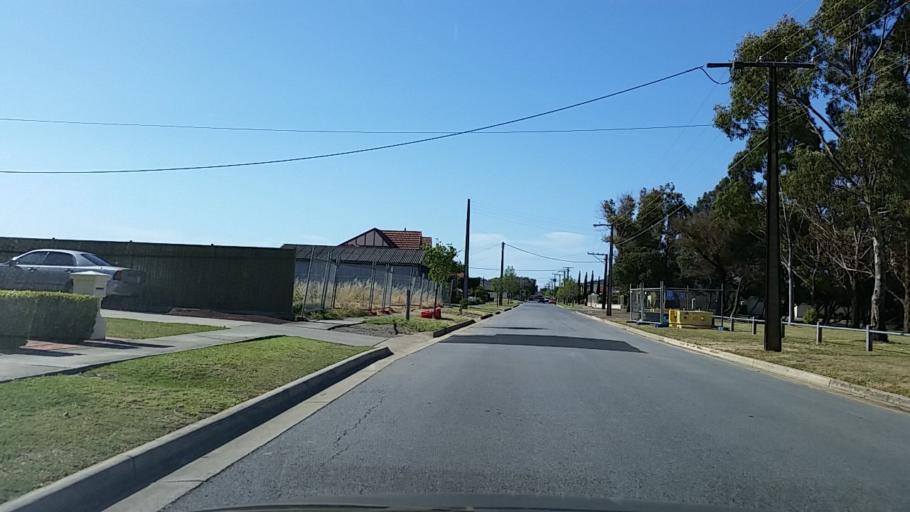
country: AU
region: South Australia
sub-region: Charles Sturt
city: Henley Beach
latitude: -34.9176
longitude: 138.5083
